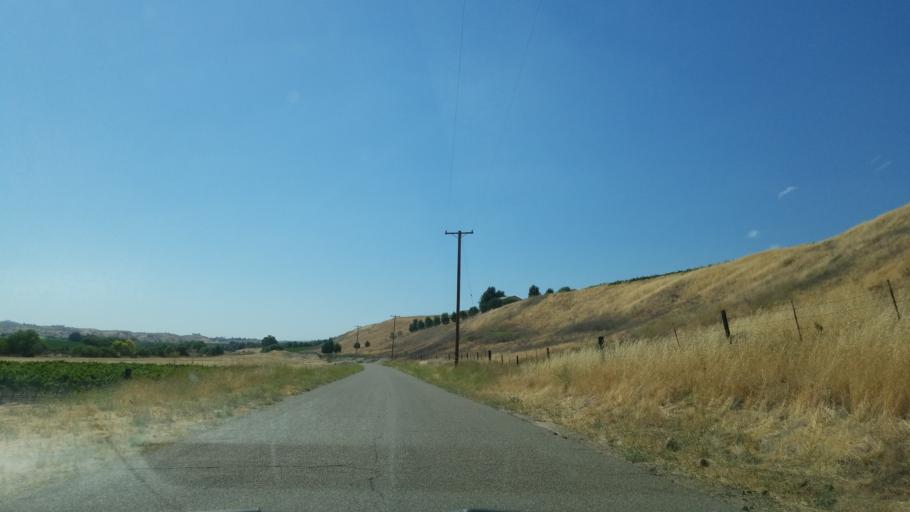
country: US
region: California
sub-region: San Luis Obispo County
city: San Miguel
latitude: 35.7304
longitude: -120.6568
